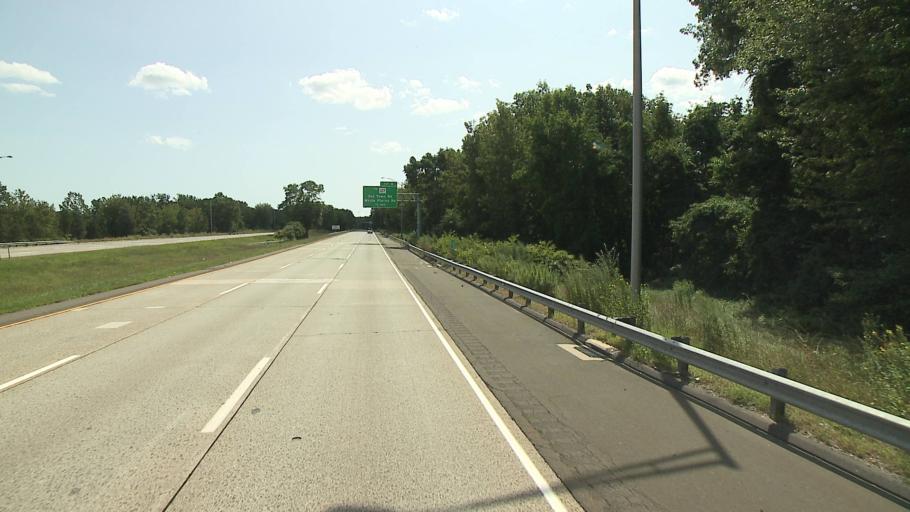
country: US
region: Connecticut
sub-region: Fairfield County
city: Trumbull
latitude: 41.2290
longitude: -73.1868
